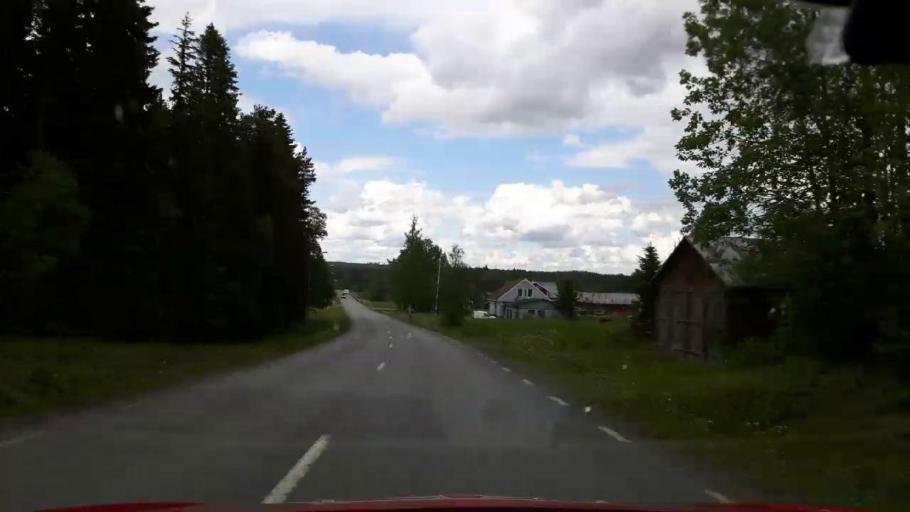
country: SE
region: Jaemtland
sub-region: Krokoms Kommun
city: Krokom
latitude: 63.5466
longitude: 14.2779
